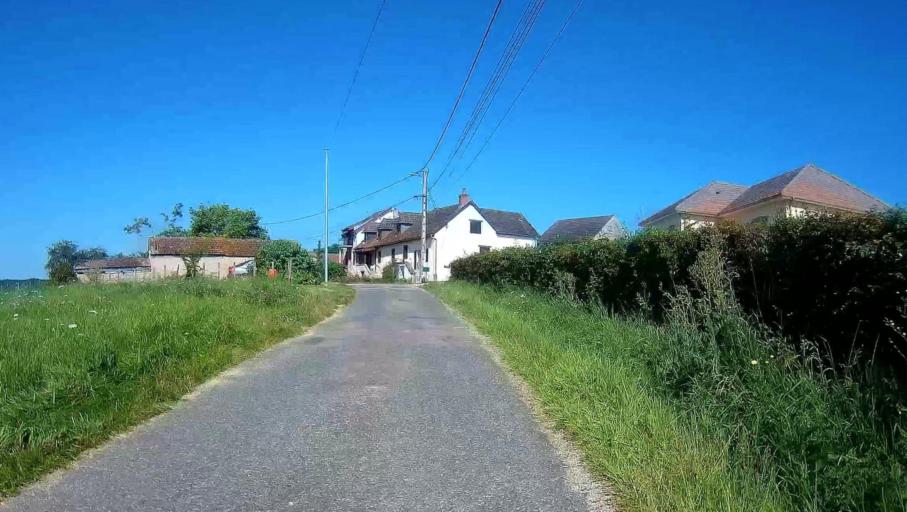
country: FR
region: Bourgogne
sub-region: Departement de Saone-et-Loire
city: Couches
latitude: 46.8418
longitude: 4.5788
